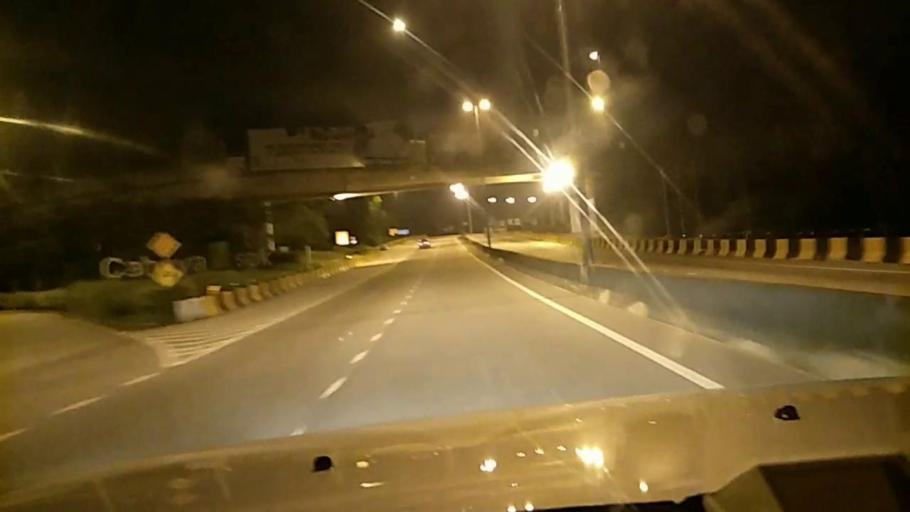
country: MY
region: Selangor
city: Kampung Baru Subang
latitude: 3.1338
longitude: 101.5001
